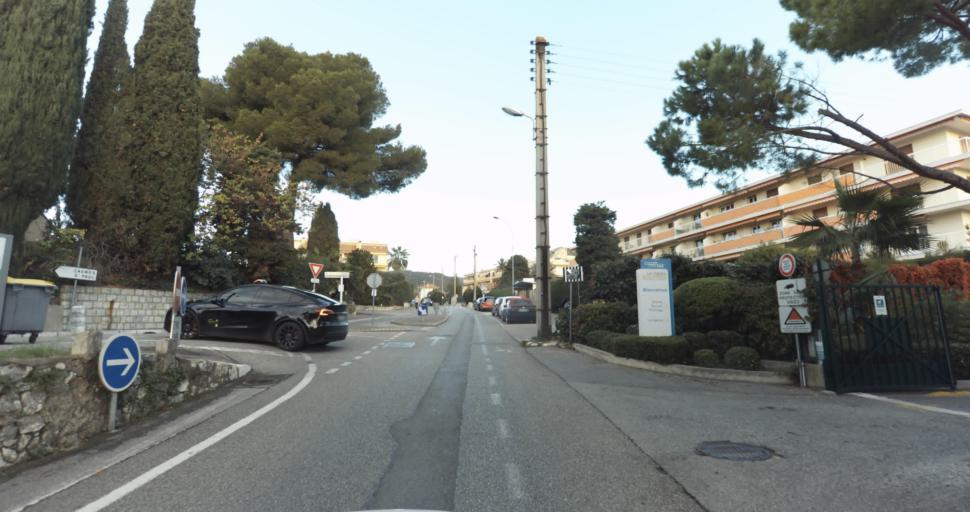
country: FR
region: Provence-Alpes-Cote d'Azur
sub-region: Departement des Alpes-Maritimes
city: Vence
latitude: 43.7178
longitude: 7.1195
